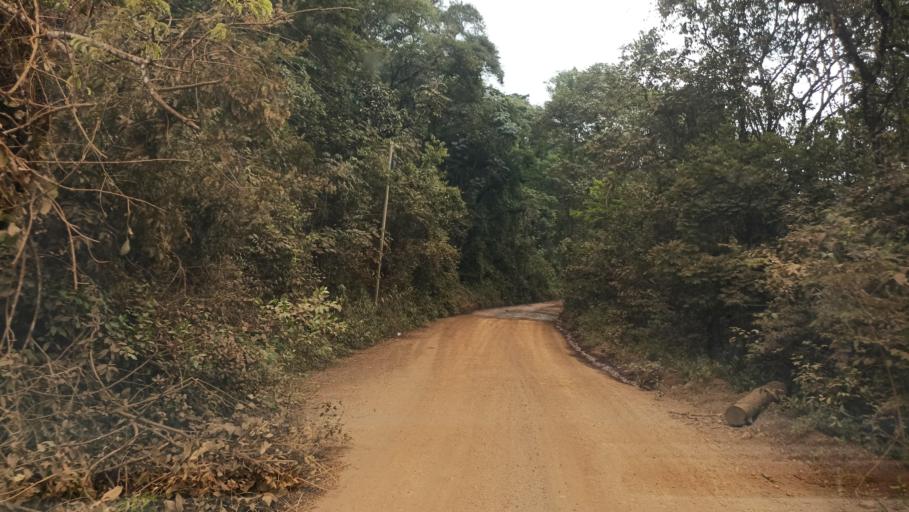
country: BR
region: Minas Gerais
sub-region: Itabirito
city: Itabirito
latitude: -20.3688
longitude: -43.7614
